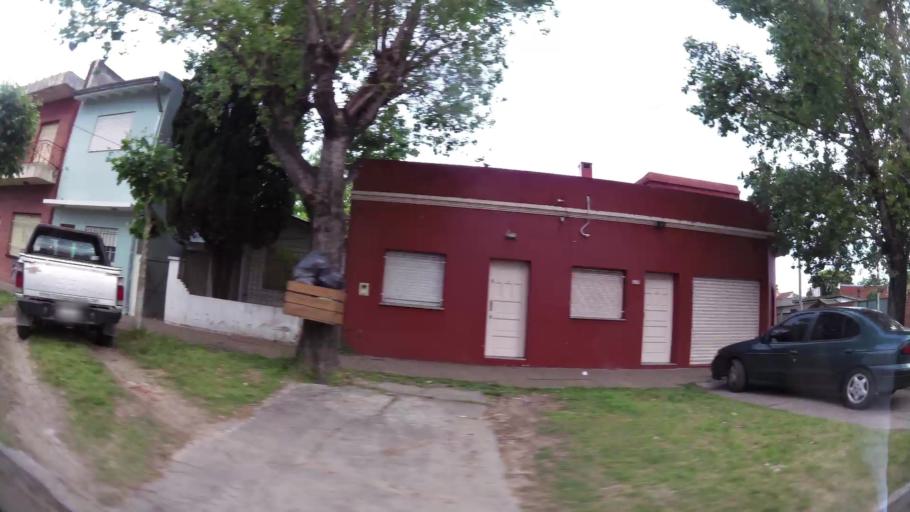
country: AR
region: Buenos Aires
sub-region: Partido de Quilmes
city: Quilmes
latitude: -34.7527
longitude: -58.2277
